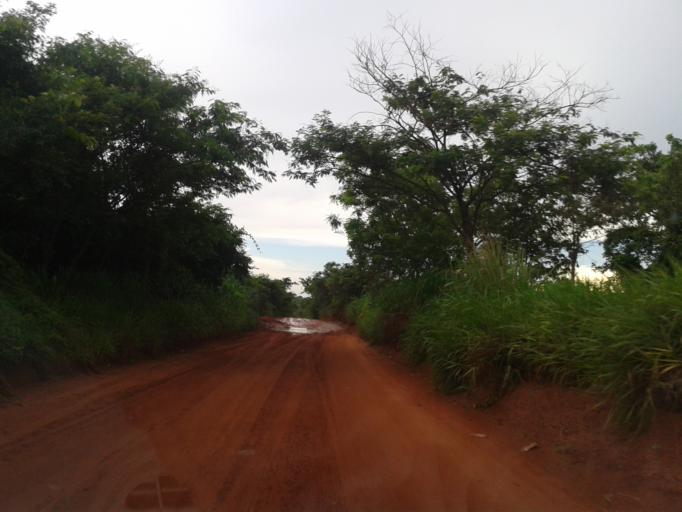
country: BR
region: Minas Gerais
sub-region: Santa Vitoria
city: Santa Vitoria
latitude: -19.1172
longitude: -50.5312
